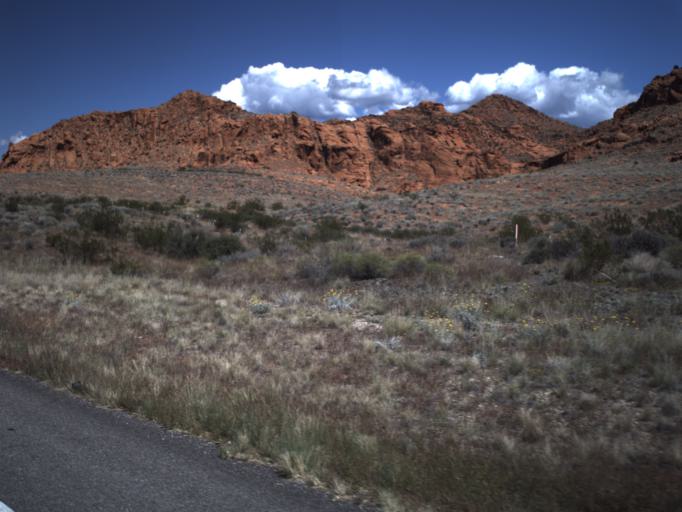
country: US
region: Utah
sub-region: Washington County
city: Saint George
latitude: 37.1420
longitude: -113.6049
